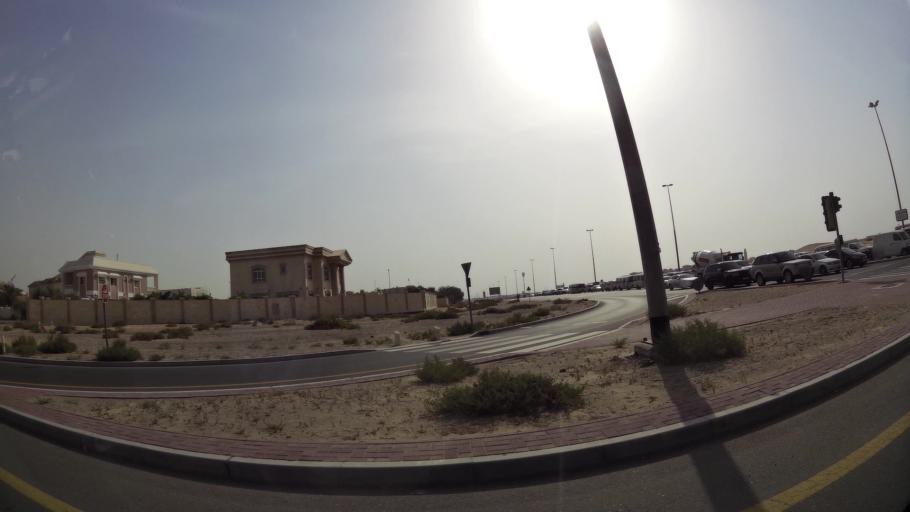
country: AE
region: Ash Shariqah
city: Sharjah
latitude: 25.2549
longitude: 55.4297
